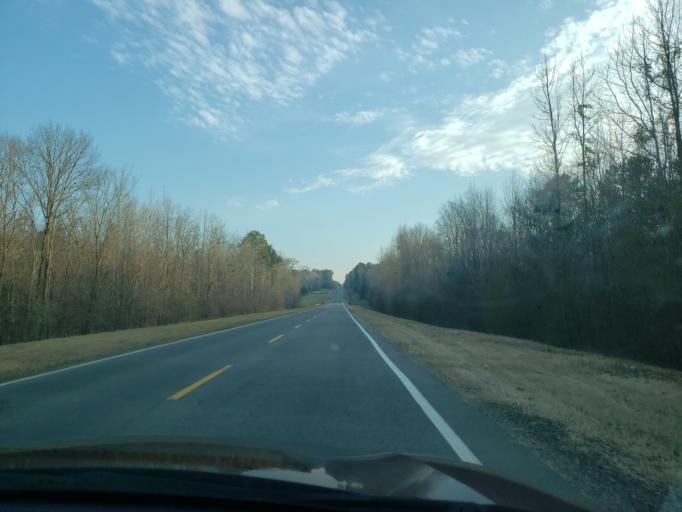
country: US
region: Alabama
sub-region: Hale County
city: Greensboro
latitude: 32.7628
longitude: -87.5854
